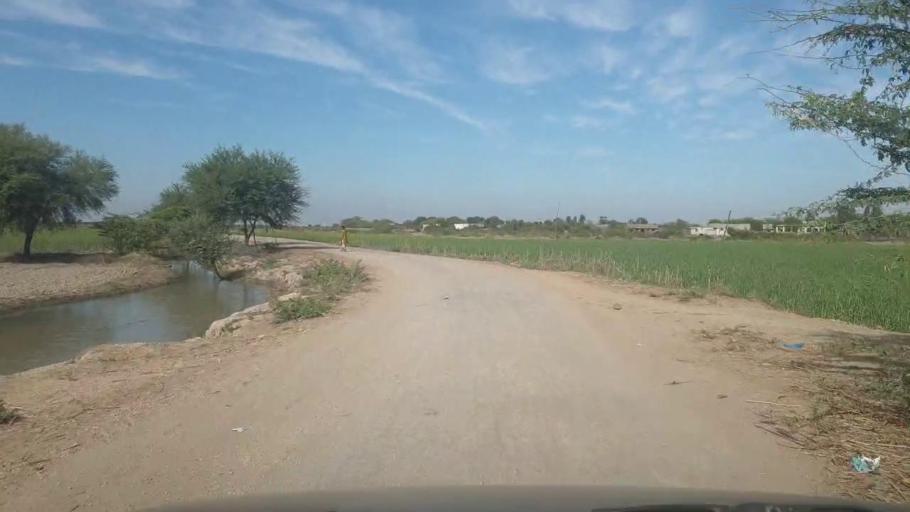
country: PK
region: Sindh
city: Mirwah Gorchani
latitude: 25.4323
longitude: 69.2040
